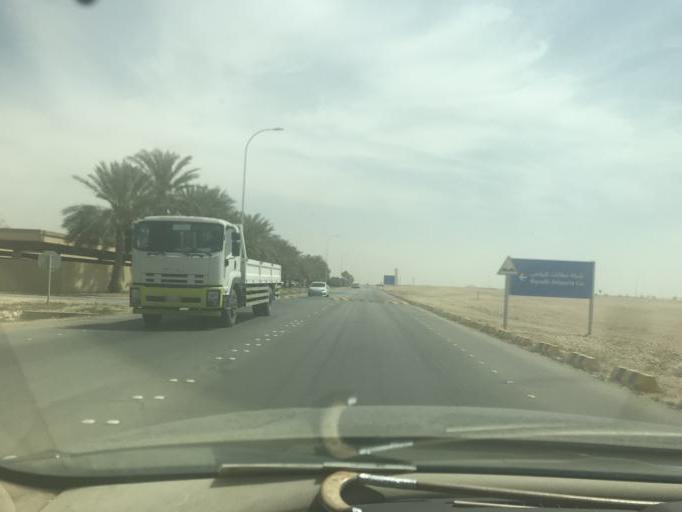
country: SA
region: Ar Riyad
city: Riyadh
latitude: 24.9761
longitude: 46.6884
